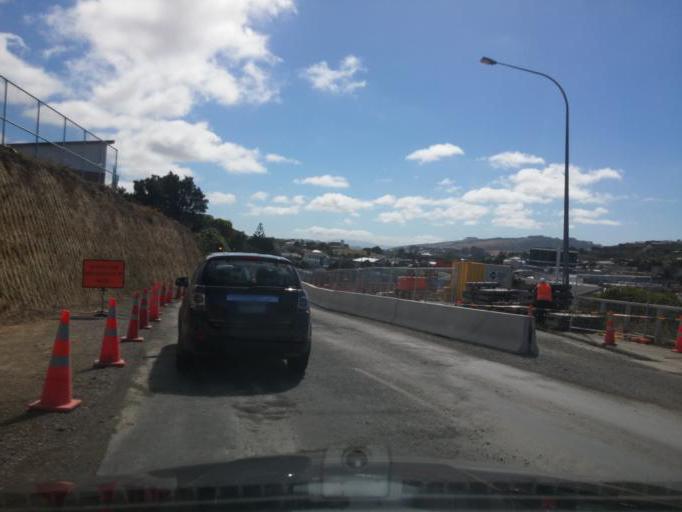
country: NZ
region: Wellington
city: Petone
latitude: -41.2250
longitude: 174.8032
